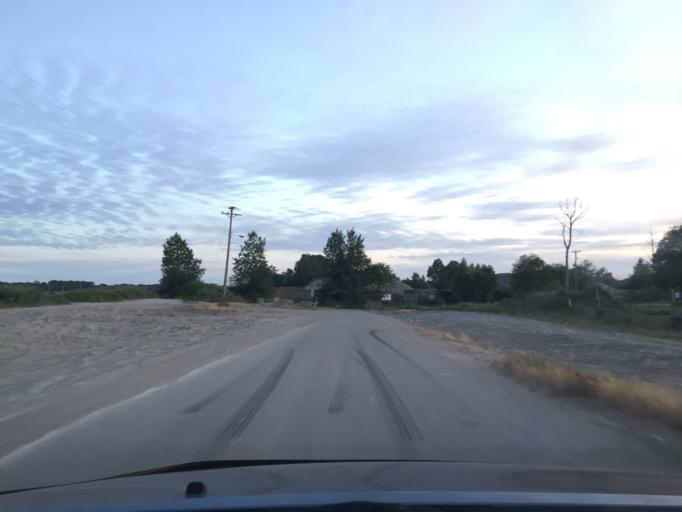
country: CA
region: British Columbia
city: Ladner
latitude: 49.1417
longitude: -123.0545
